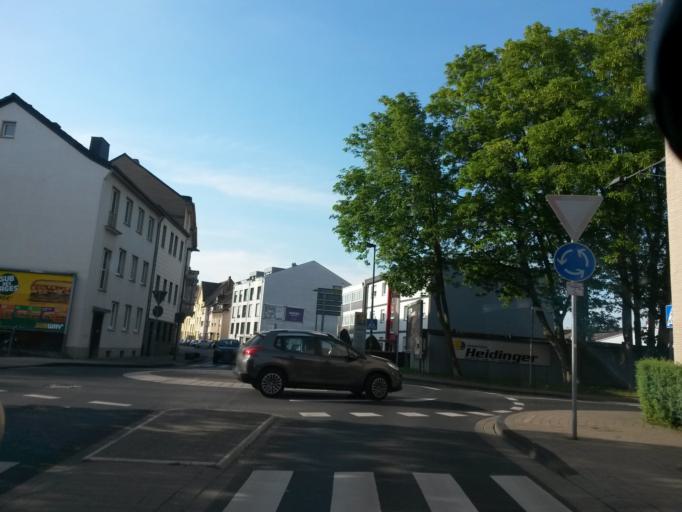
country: DE
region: North Rhine-Westphalia
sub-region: Regierungsbezirk Koln
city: Siegburg
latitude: 50.7978
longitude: 7.2028
